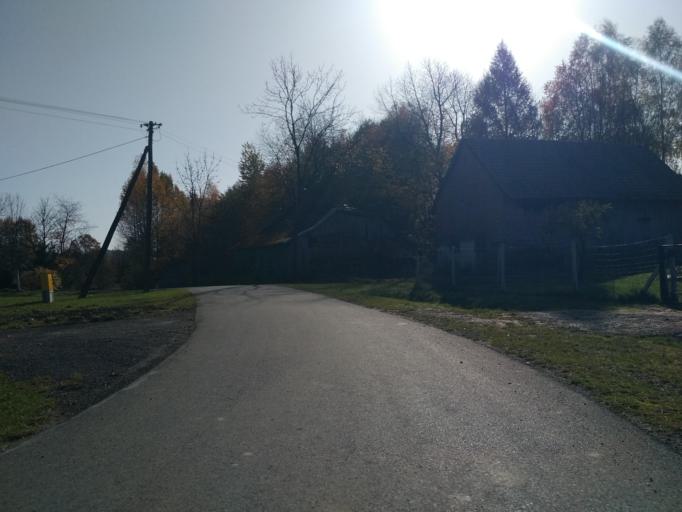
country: PL
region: Subcarpathian Voivodeship
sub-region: Powiat rzeszowski
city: Blazowa
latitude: 49.8625
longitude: 22.1245
